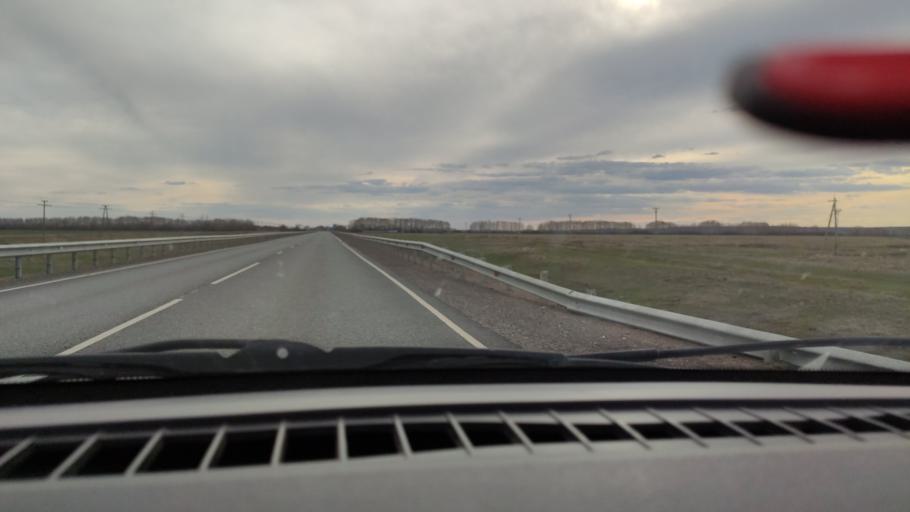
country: RU
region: Bashkortostan
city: Mayachnyy
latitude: 52.3911
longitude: 55.6801
